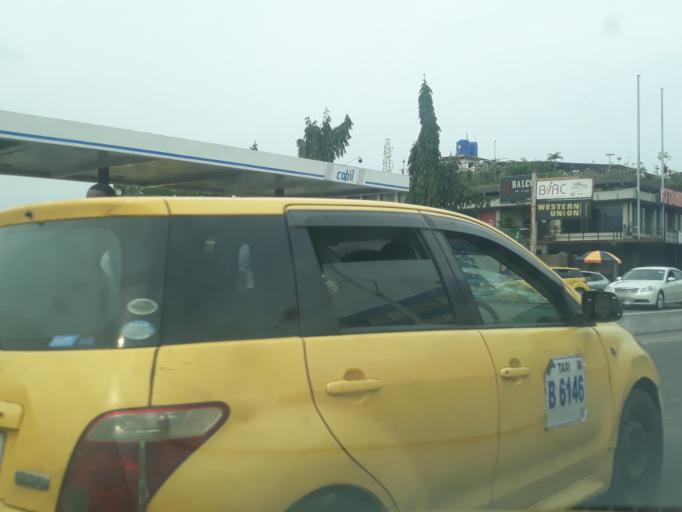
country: CD
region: Kinshasa
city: Kinshasa
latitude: -4.3335
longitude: 15.2584
